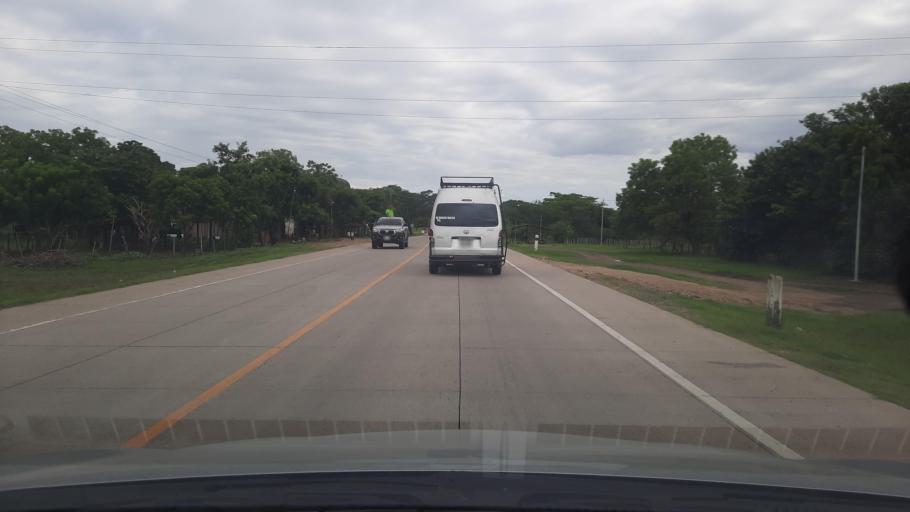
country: NI
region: Chinandega
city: Somotillo
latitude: 12.8738
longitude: -86.8519
